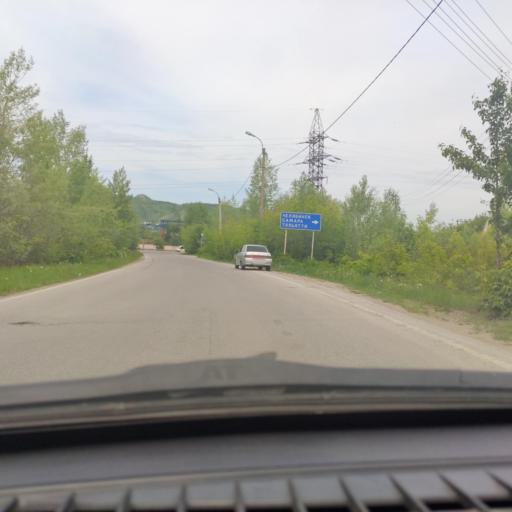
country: RU
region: Samara
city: Zhigulevsk
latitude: 53.4116
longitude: 49.4832
